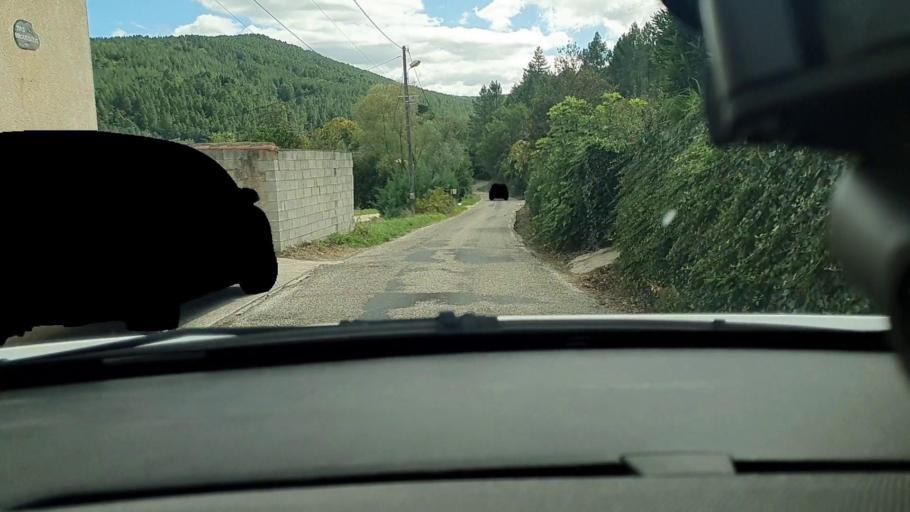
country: FR
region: Languedoc-Roussillon
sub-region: Departement du Gard
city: Branoux-les-Taillades
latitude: 44.2952
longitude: 4.0061
